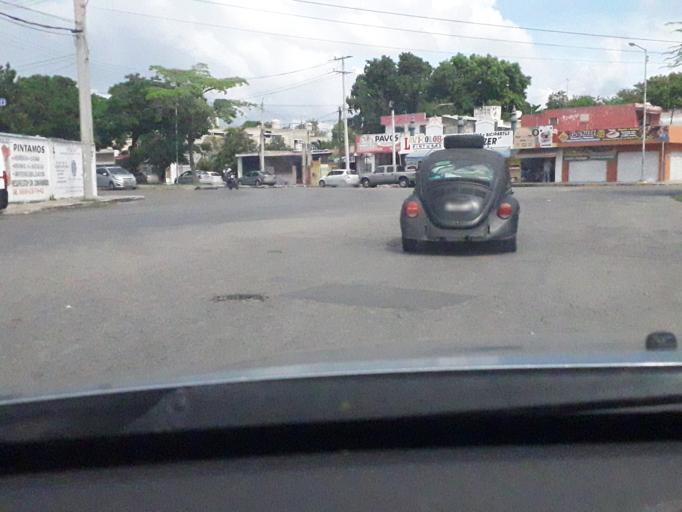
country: MX
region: Yucatan
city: Merida
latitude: 20.9720
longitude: -89.6564
